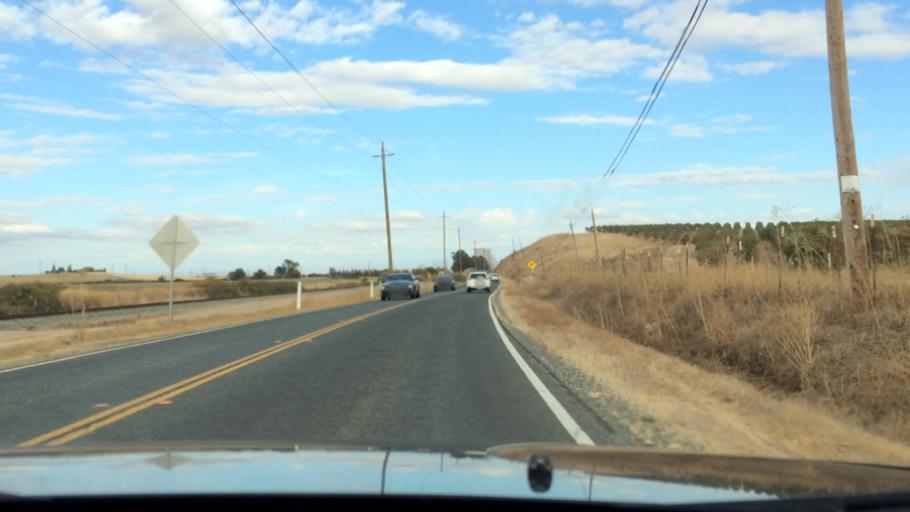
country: US
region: California
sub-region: Sacramento County
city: Clay
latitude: 38.3332
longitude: -121.1762
